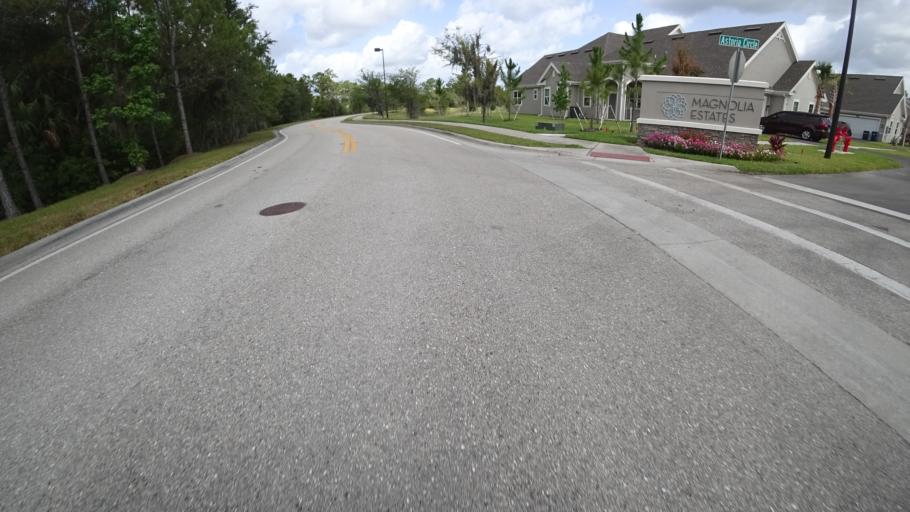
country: US
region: Florida
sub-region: Sarasota County
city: Desoto Lakes
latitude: 27.4204
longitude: -82.4554
